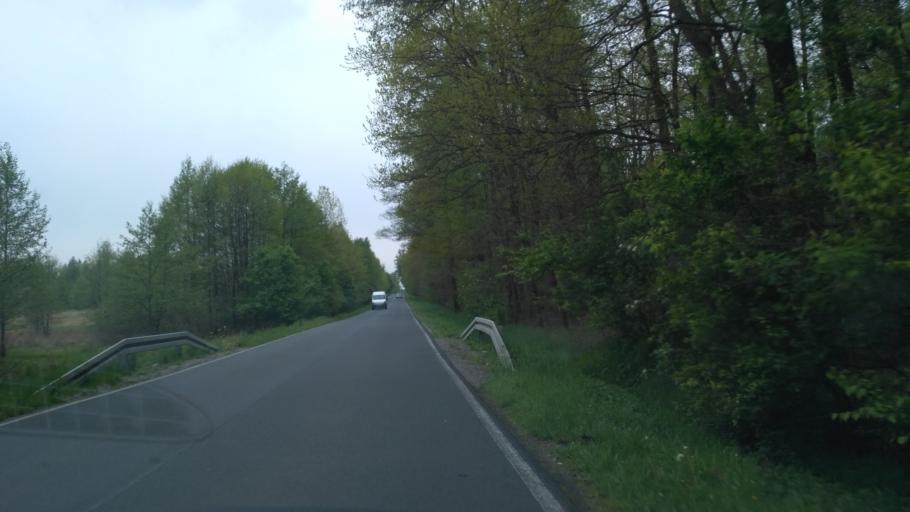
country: PL
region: Subcarpathian Voivodeship
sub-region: Powiat ropczycko-sedziszowski
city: Sedziszow Malopolski
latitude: 50.1328
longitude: 21.7540
